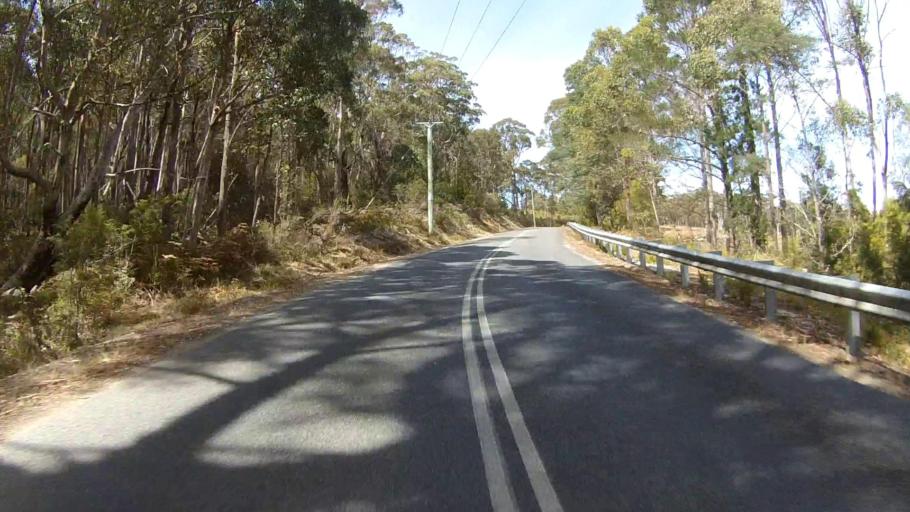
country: AU
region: Tasmania
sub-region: Huon Valley
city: Cygnet
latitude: -43.2228
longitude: 147.1283
